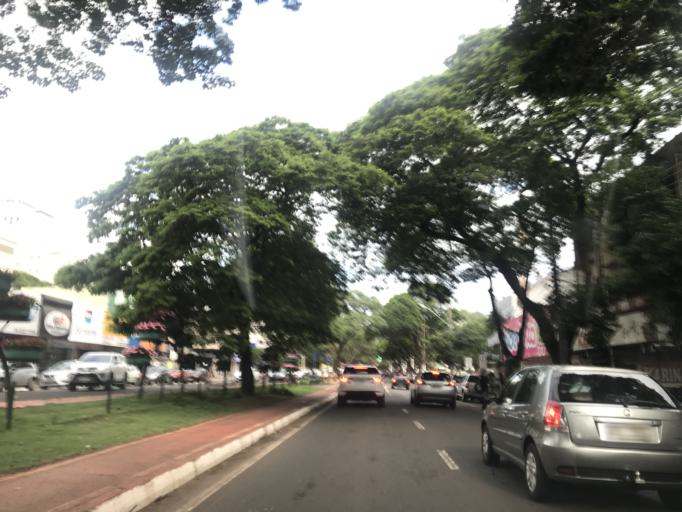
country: BR
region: Parana
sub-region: Maringa
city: Maringa
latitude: -23.4209
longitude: -51.9423
